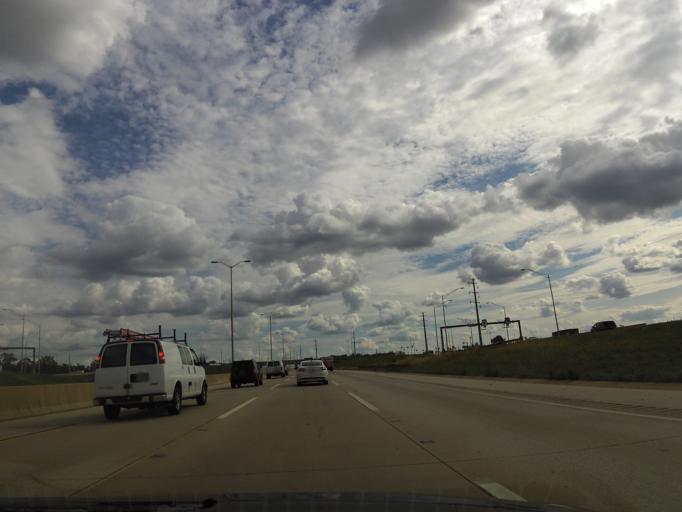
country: US
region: Illinois
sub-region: Will County
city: Lockport
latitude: 41.6015
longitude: -88.0118
